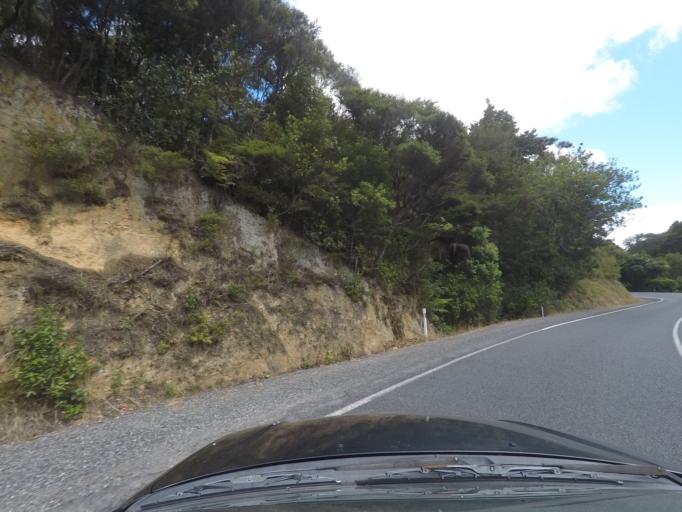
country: NZ
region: Northland
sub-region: Whangarei
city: Ruakaka
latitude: -36.0335
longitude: 174.5104
